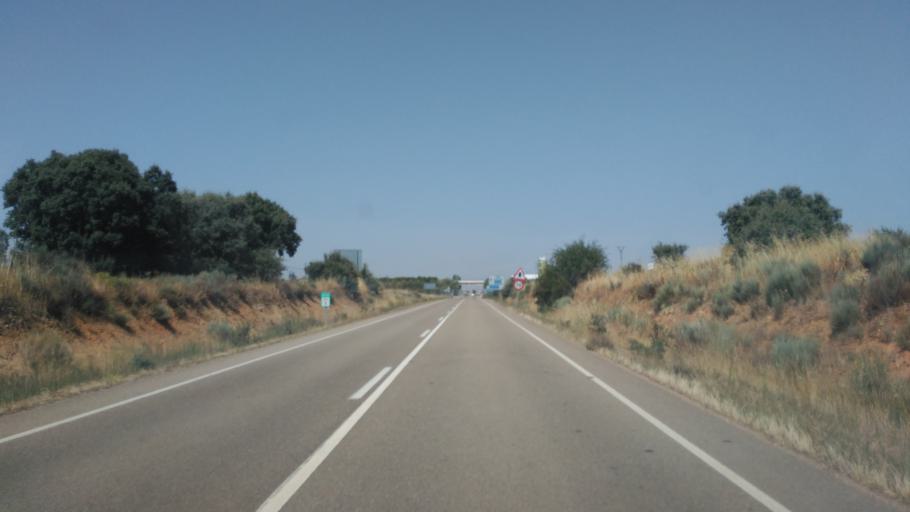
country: ES
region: Castille and Leon
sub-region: Provincia de Salamanca
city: La Fuente de San Esteban
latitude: 40.7845
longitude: -6.2371
